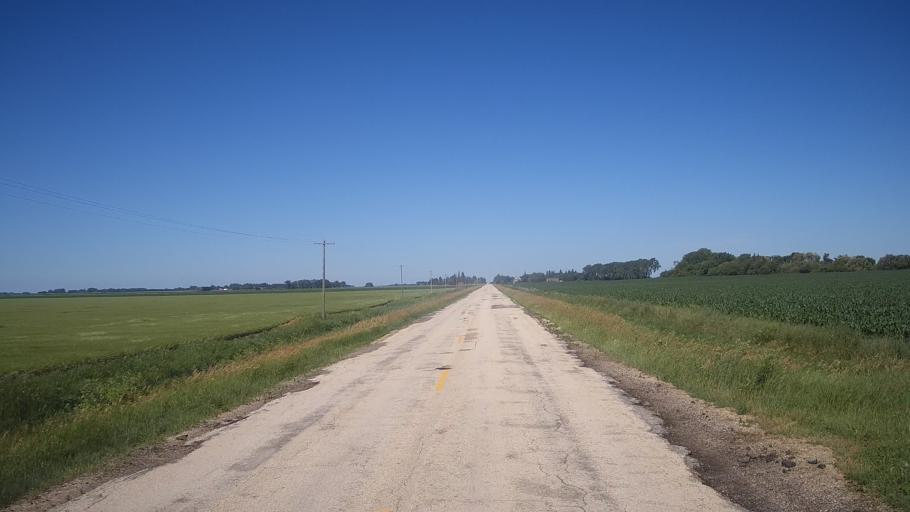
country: CA
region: Manitoba
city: Portage la Prairie
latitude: 50.0437
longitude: -98.0396
